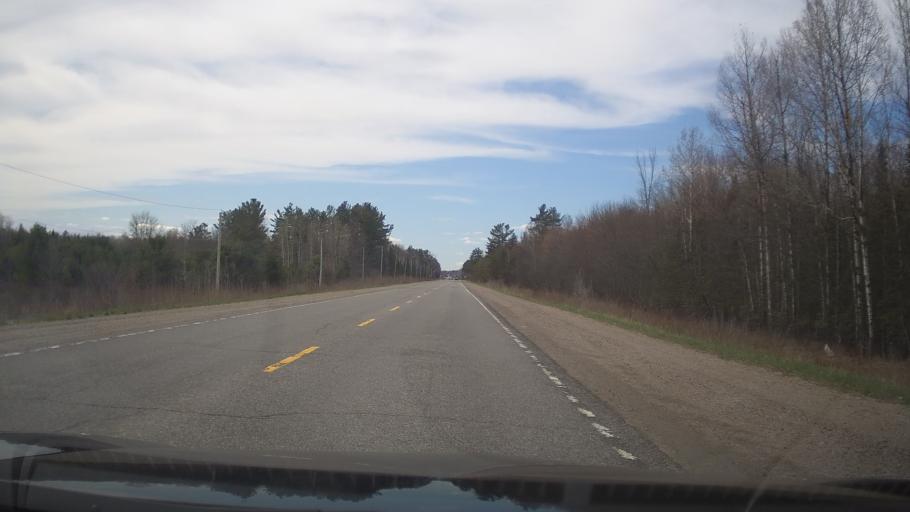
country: CA
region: Ontario
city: Arnprior
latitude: 45.5302
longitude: -76.3074
